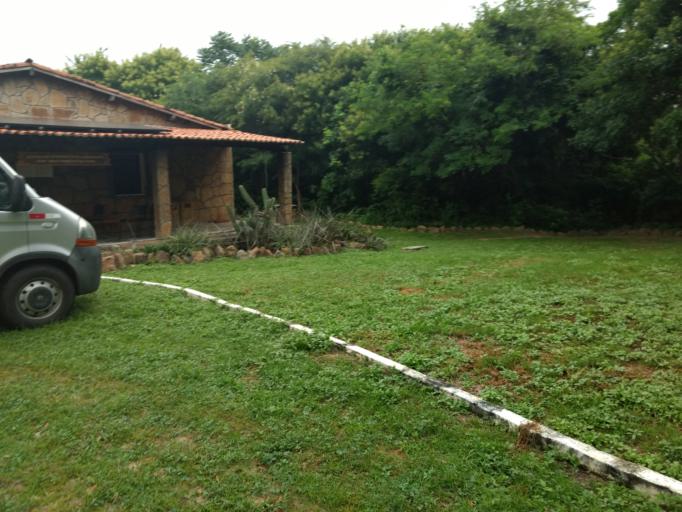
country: BR
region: Ceara
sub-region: Crateus
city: Crateus
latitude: -5.1417
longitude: -40.9164
